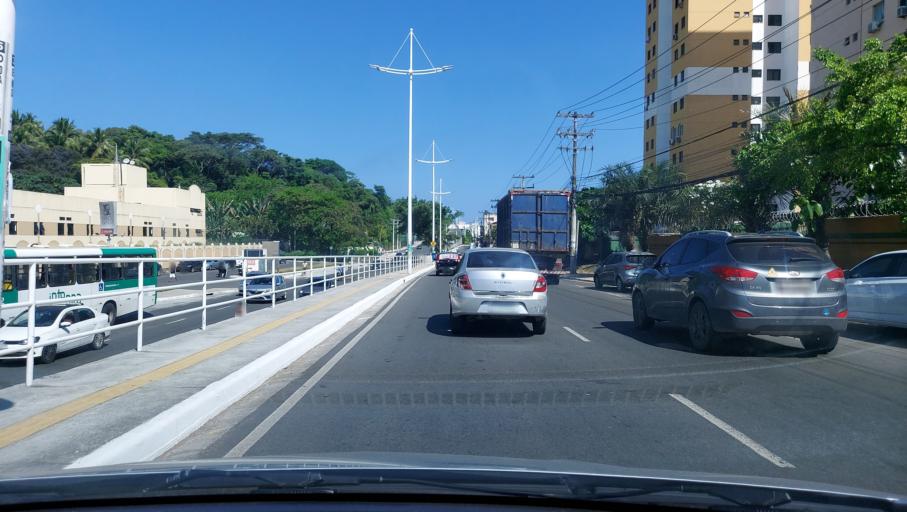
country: BR
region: Bahia
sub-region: Salvador
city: Salvador
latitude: -12.9610
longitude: -38.4389
